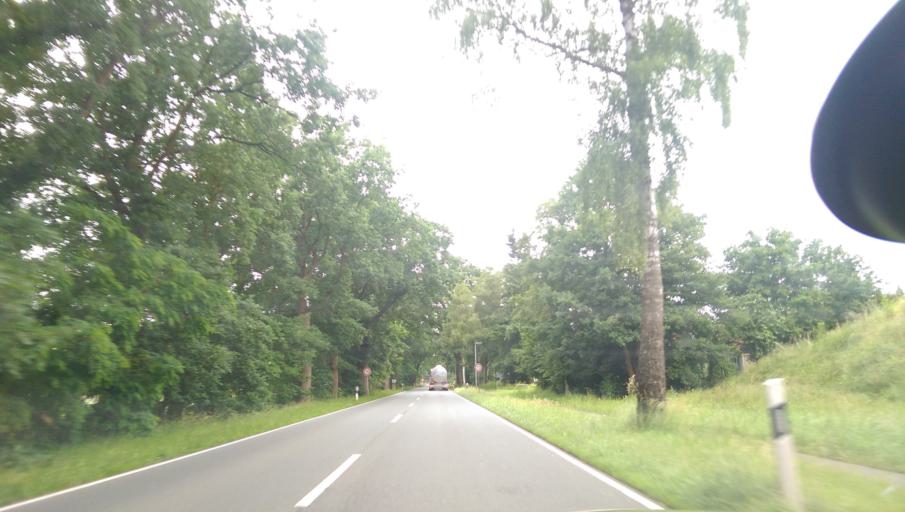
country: DE
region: Lower Saxony
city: Rotenburg
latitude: 53.0947
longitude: 9.4088
